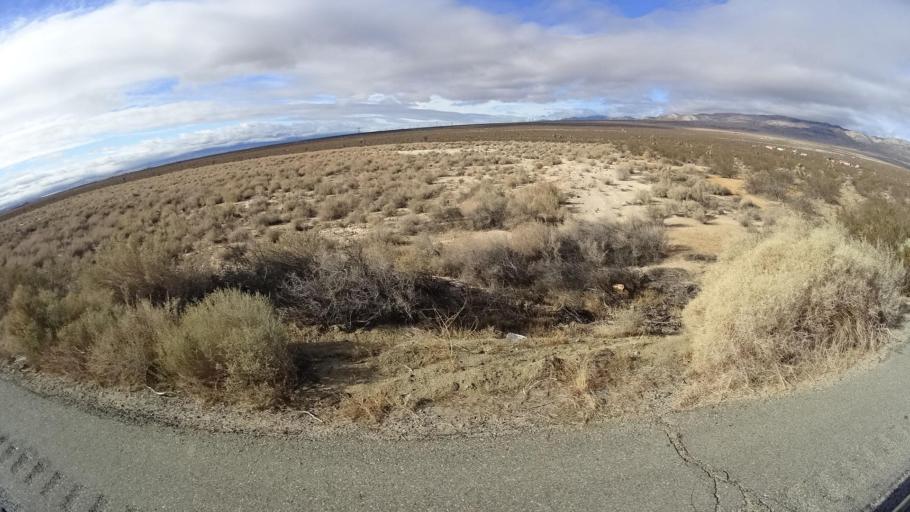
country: US
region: California
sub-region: Kern County
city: Mojave
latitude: 34.9581
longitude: -118.2922
